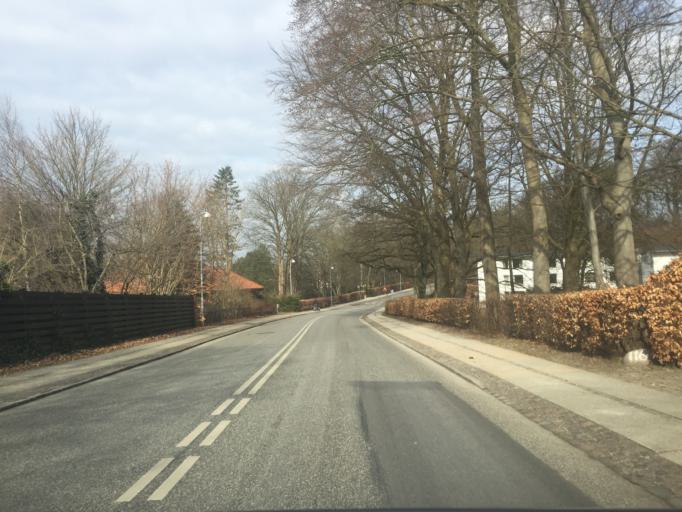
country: DK
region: Capital Region
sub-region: Lyngby-Tarbaek Kommune
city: Kongens Lyngby
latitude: 55.7889
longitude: 12.5026
